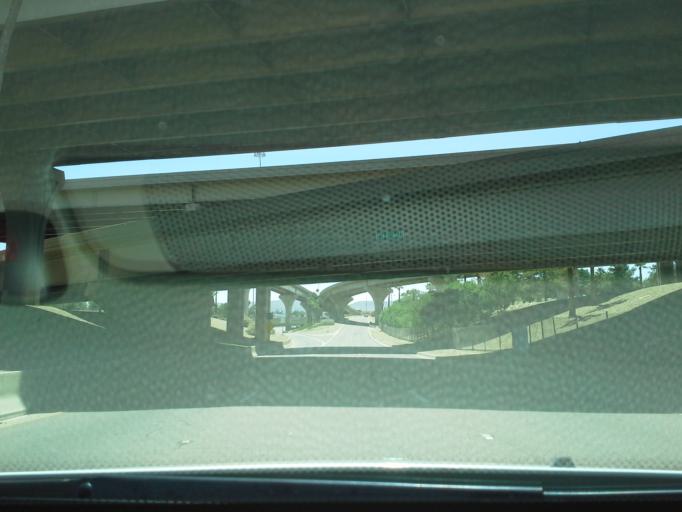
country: US
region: Arizona
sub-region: Maricopa County
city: Phoenix
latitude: 33.4623
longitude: -112.1094
